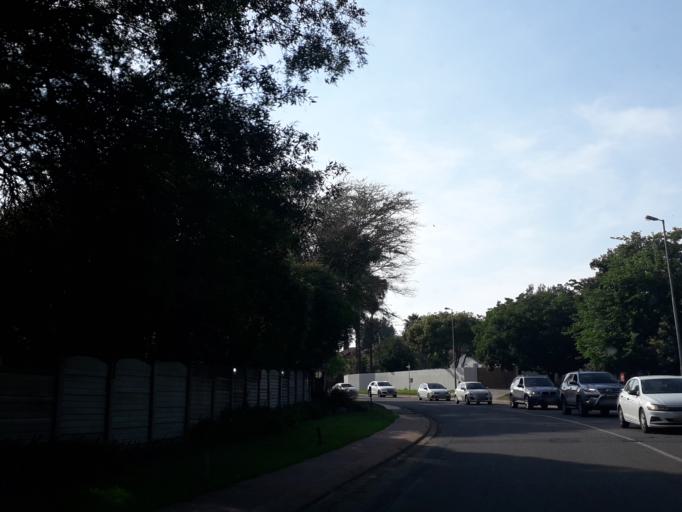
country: ZA
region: Gauteng
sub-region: City of Johannesburg Metropolitan Municipality
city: Diepsloot
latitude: -26.0344
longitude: 28.0166
